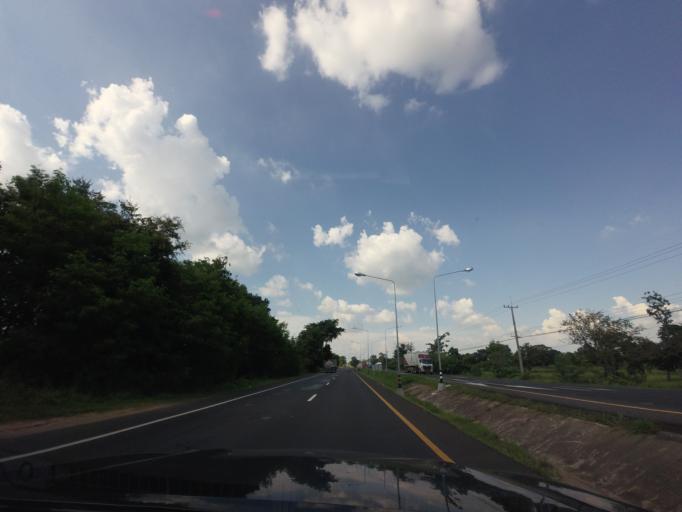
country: TH
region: Nakhon Ratchasima
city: Bua Lai
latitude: 15.7047
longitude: 102.5855
